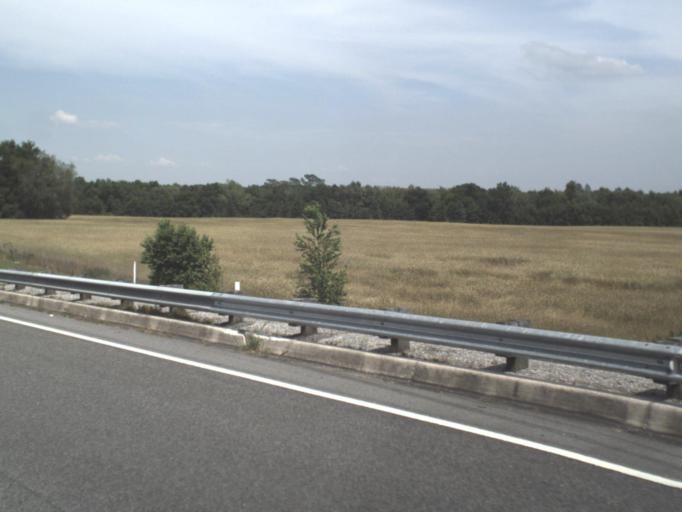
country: US
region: Florida
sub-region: Suwannee County
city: Live Oak
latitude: 30.3450
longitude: -83.0873
